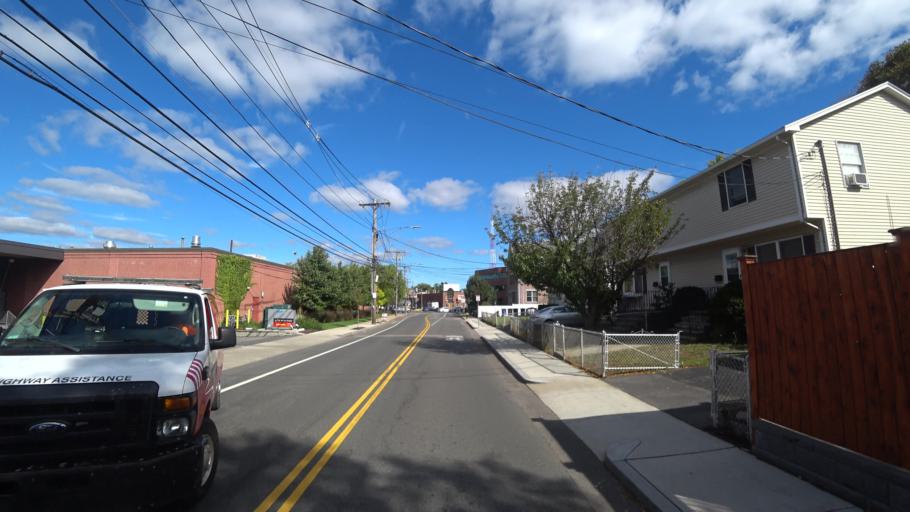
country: US
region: Massachusetts
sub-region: Middlesex County
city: Cambridge
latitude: 42.3621
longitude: -71.1357
